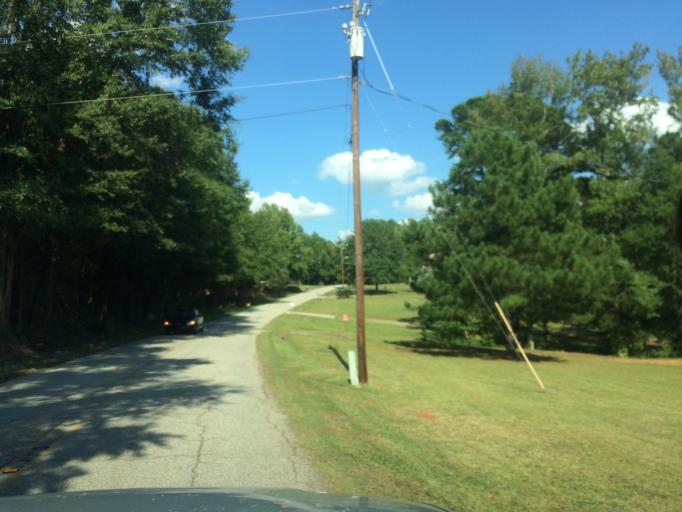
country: US
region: South Carolina
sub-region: Greenwood County
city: Ware Shoals
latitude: 34.4347
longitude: -82.2584
